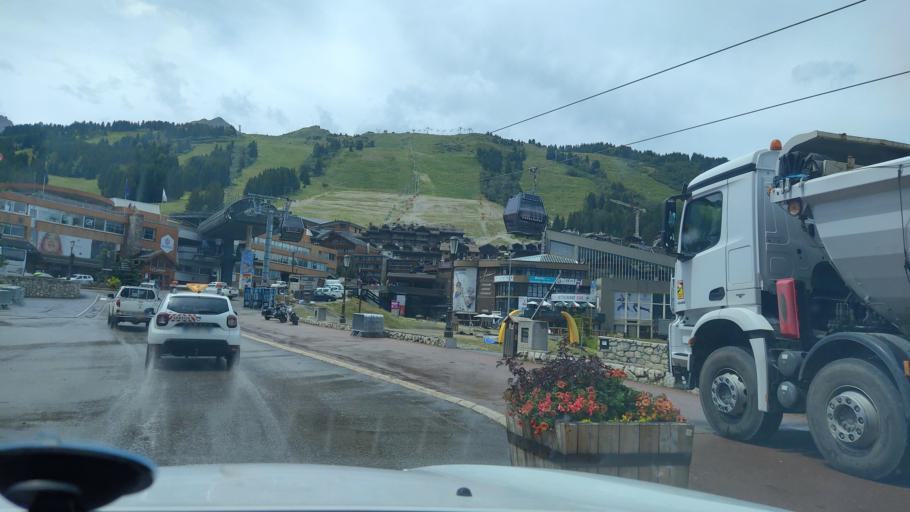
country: FR
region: Rhone-Alpes
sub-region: Departement de la Savoie
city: Courchevel
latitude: 45.4158
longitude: 6.6347
